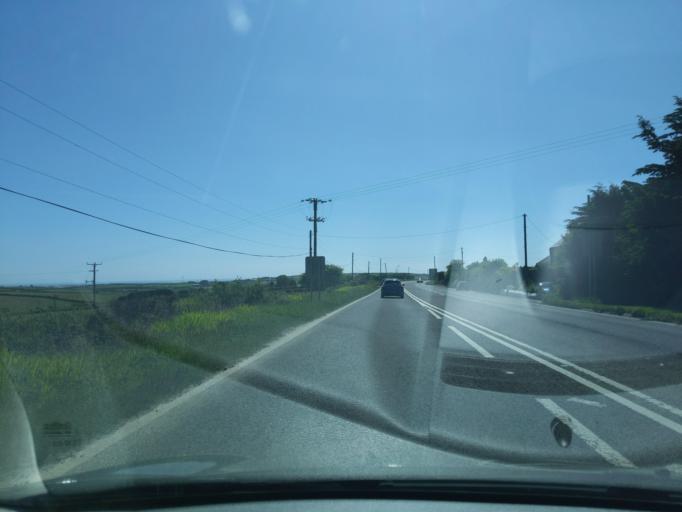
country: GB
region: England
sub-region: Cornwall
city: Wendron
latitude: 50.1520
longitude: -5.1964
